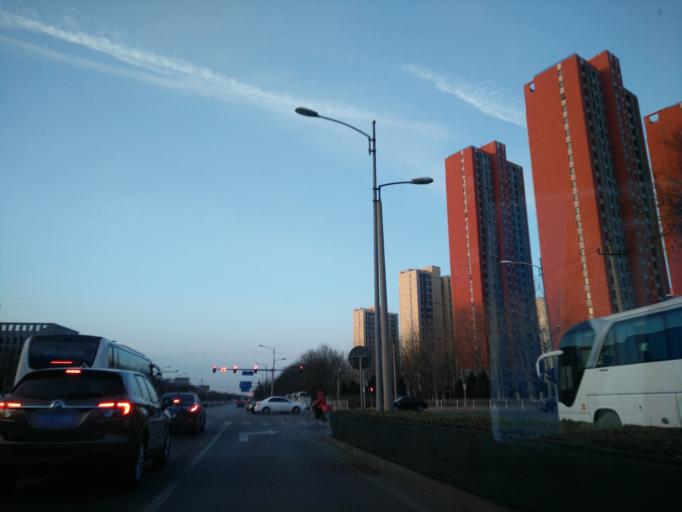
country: CN
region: Beijing
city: Jiugong
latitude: 39.7631
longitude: 116.5070
